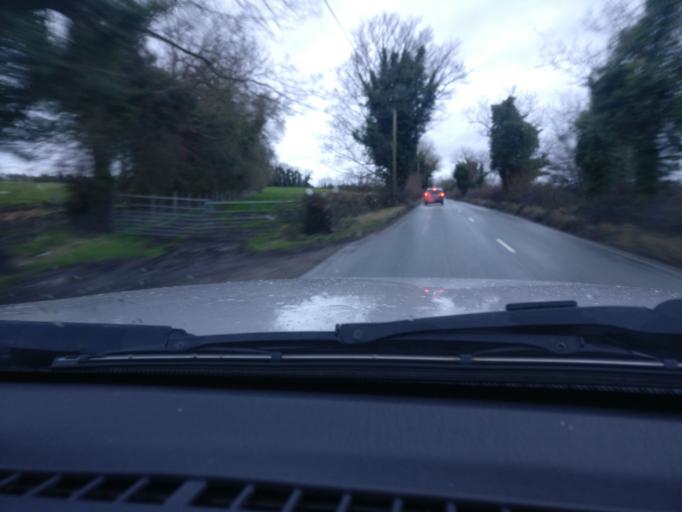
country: IE
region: Leinster
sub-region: An Mhi
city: Longwood
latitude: 53.4785
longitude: -6.8995
